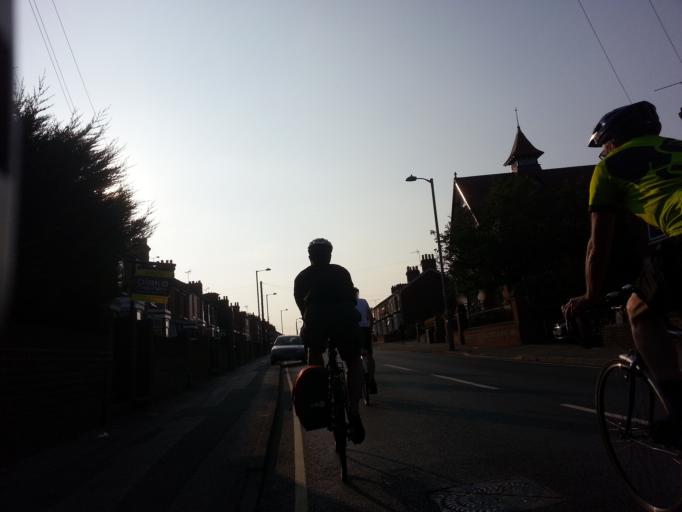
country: GB
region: England
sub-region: Suffolk
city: Ipswich
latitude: 52.0657
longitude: 1.1307
